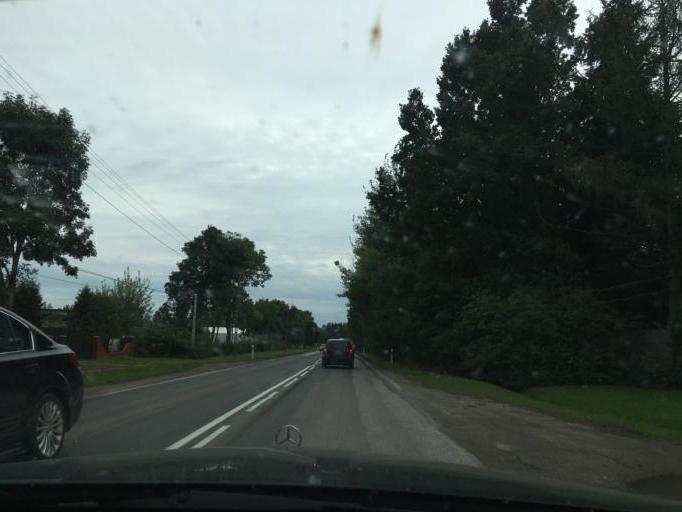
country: PL
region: Masovian Voivodeship
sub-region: Powiat ostrowski
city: Ostrow Mazowiecka
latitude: 52.8350
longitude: 21.8728
